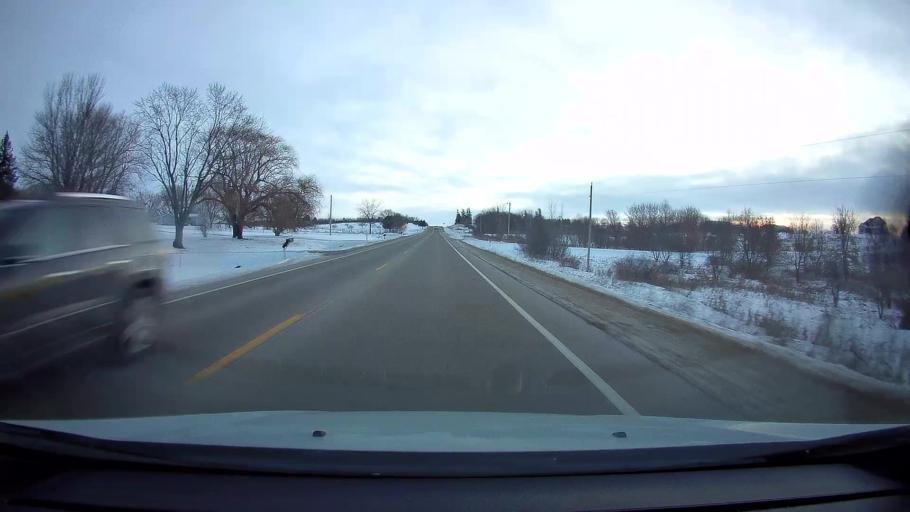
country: US
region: Wisconsin
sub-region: Saint Croix County
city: New Richmond
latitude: 45.1371
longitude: -92.5039
